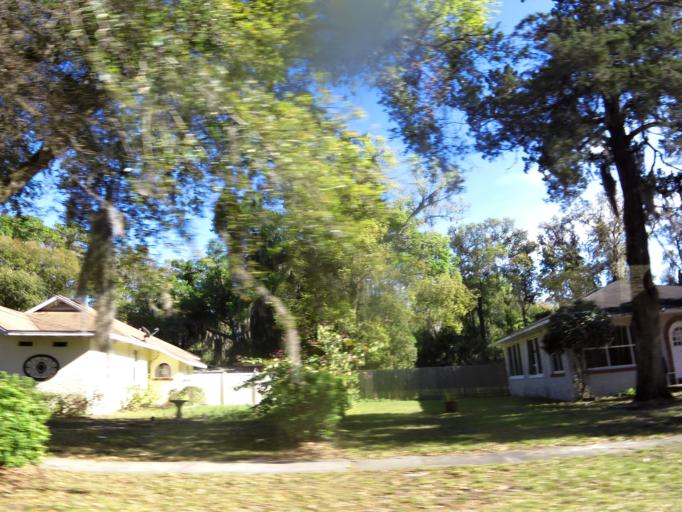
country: US
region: Florida
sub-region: Duval County
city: Jacksonville
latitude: 30.3797
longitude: -81.6473
